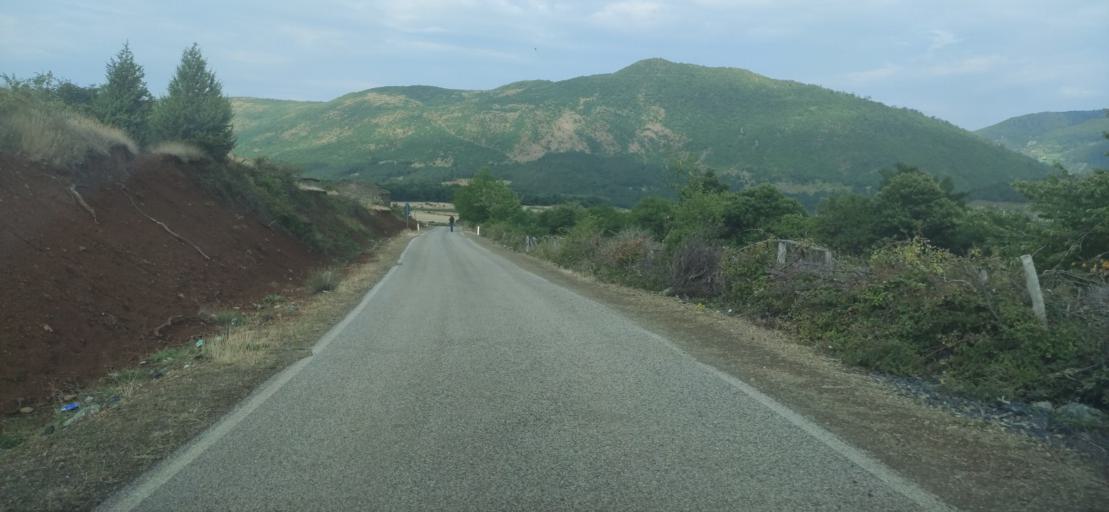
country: AL
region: Shkoder
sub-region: Rrethi i Pukes
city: Iballe
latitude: 42.1881
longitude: 20.0011
